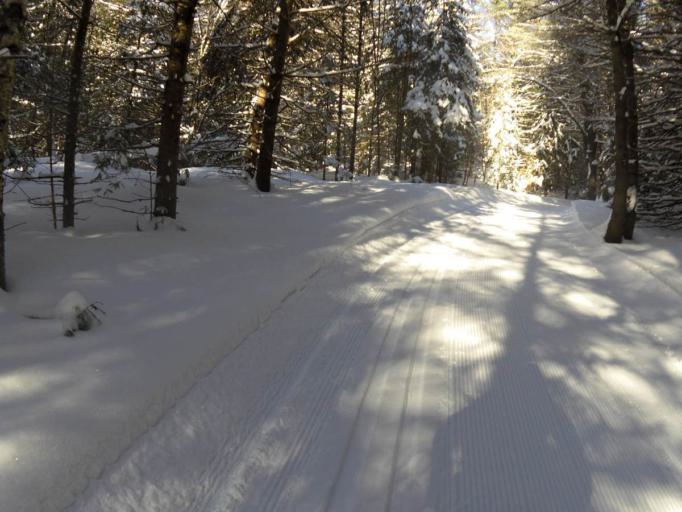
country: CA
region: Quebec
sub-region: Outaouais
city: Wakefield
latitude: 45.6235
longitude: -75.9477
